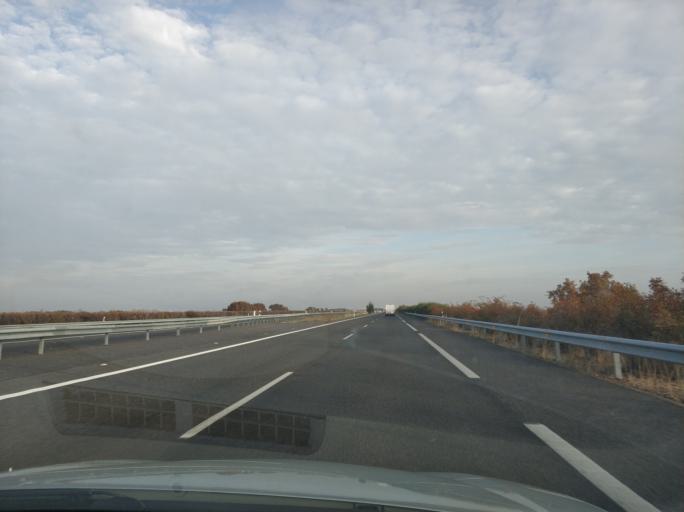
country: ES
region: Castille and Leon
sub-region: Provincia de Palencia
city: Bustillo del Paramo de Carrion
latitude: 42.3539
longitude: -4.7638
